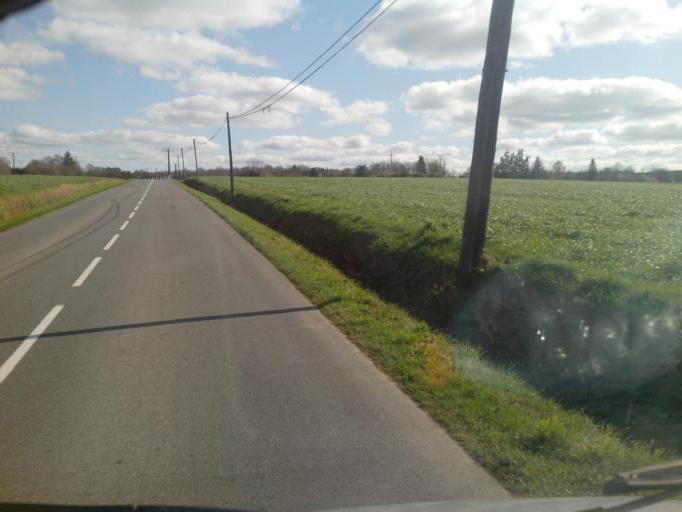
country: FR
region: Brittany
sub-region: Departement d'Ille-et-Vilaine
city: Paimpont
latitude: 48.0422
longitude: -2.1837
